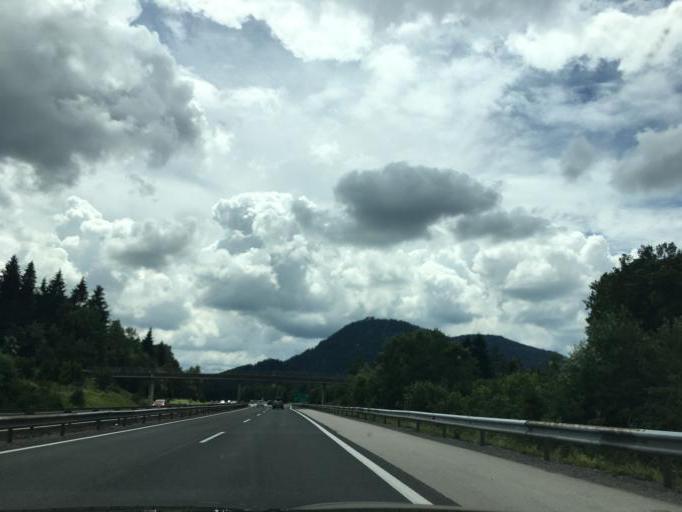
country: SI
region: Vodice
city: Vodice
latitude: 46.1502
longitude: 14.4773
